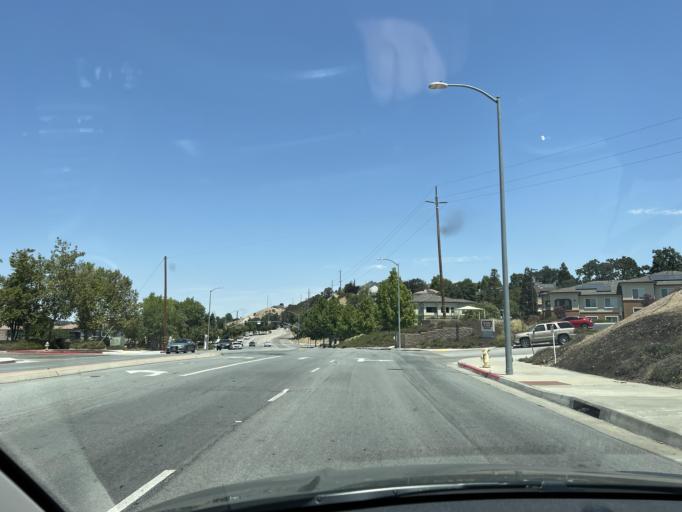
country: US
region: California
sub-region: San Luis Obispo County
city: Paso Robles
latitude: 35.6165
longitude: -120.6803
